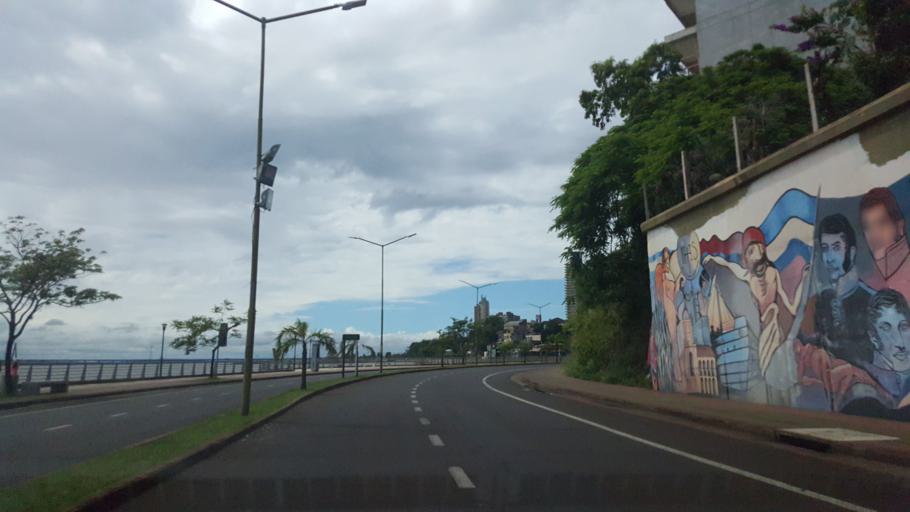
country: AR
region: Misiones
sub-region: Departamento de Capital
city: Posadas
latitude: -27.3561
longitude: -55.8913
